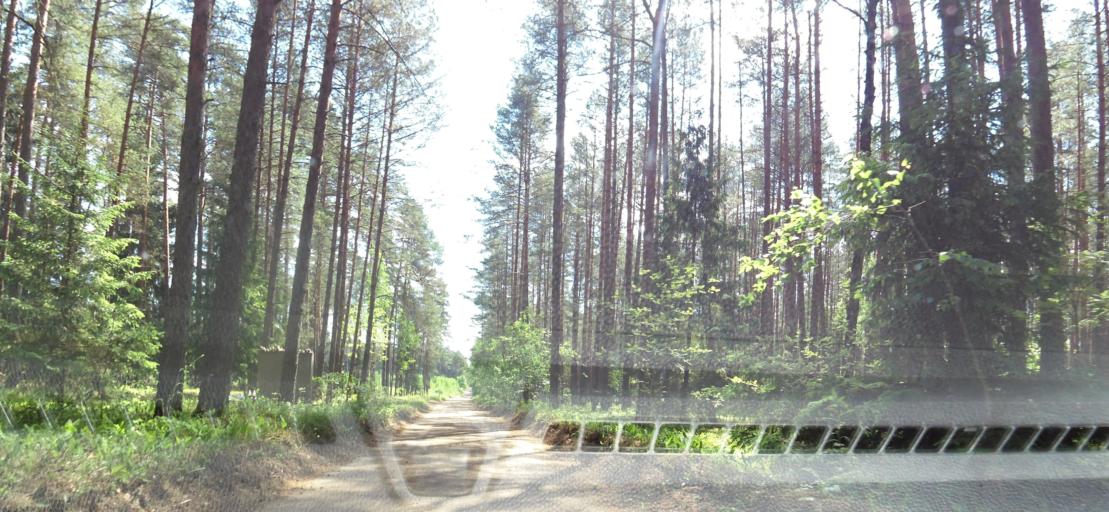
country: LT
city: Nemencine
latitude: 54.8318
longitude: 25.4354
